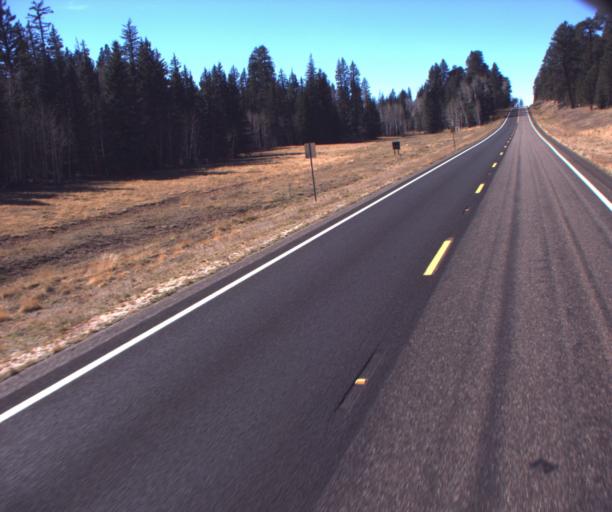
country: US
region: Arizona
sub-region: Coconino County
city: Grand Canyon
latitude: 36.5426
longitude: -112.1657
